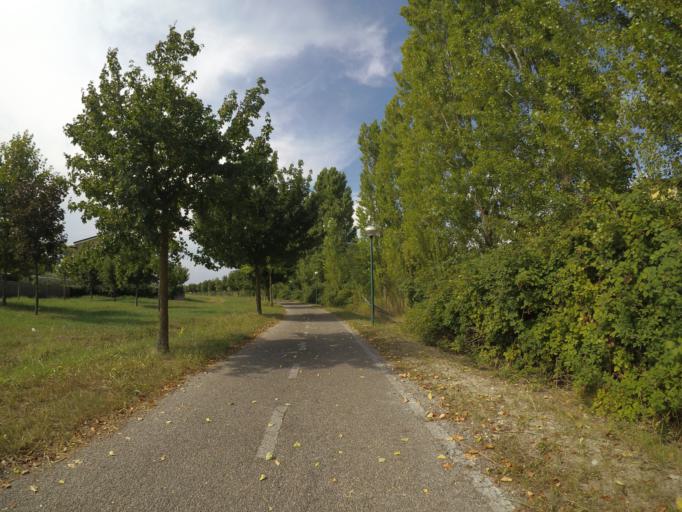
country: IT
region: Friuli Venezia Giulia
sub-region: Provincia di Udine
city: Lignano Sabbiadoro
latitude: 45.6636
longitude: 13.0745
